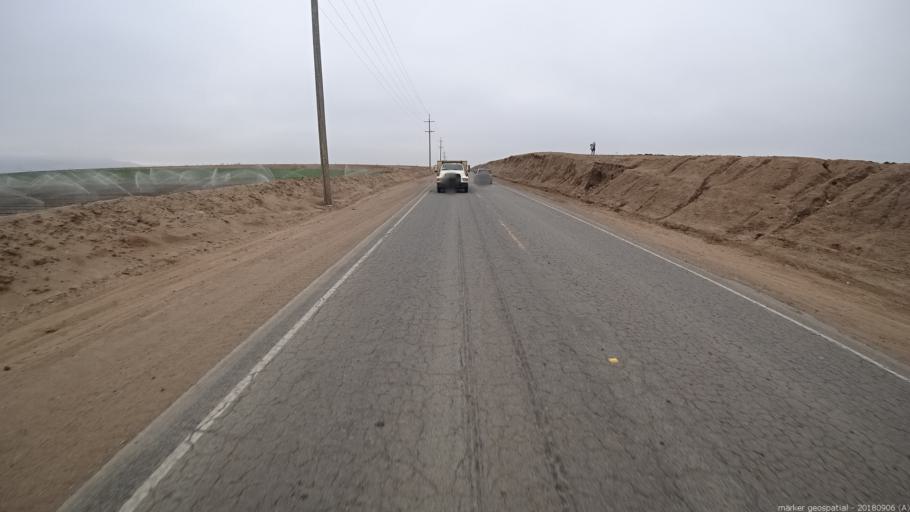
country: US
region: California
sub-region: Monterey County
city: Salinas
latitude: 36.6597
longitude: -121.5895
